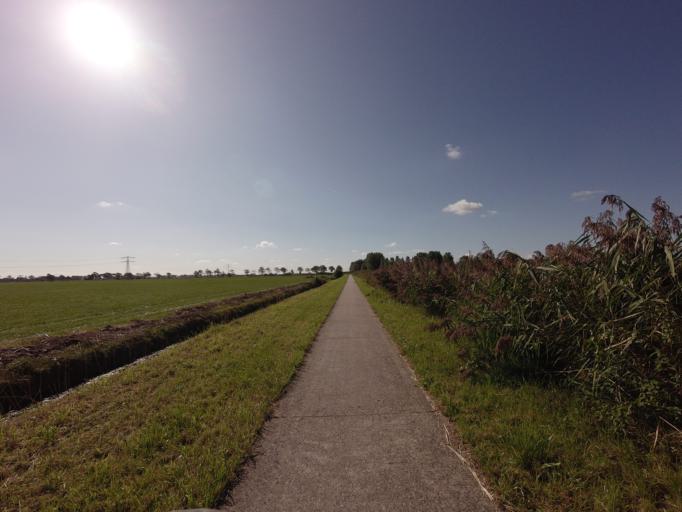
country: NL
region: Friesland
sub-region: Gemeente Leeuwarden
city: Wirdum
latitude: 53.1522
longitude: 5.7642
